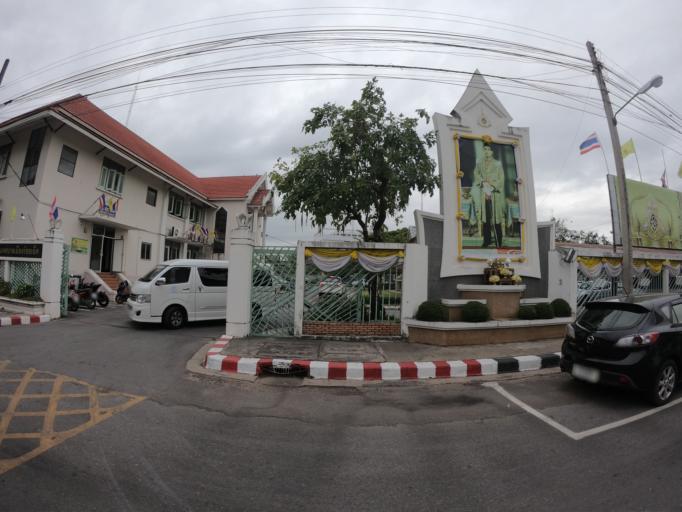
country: TH
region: Roi Et
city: Roi Et
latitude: 16.0533
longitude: 103.6515
